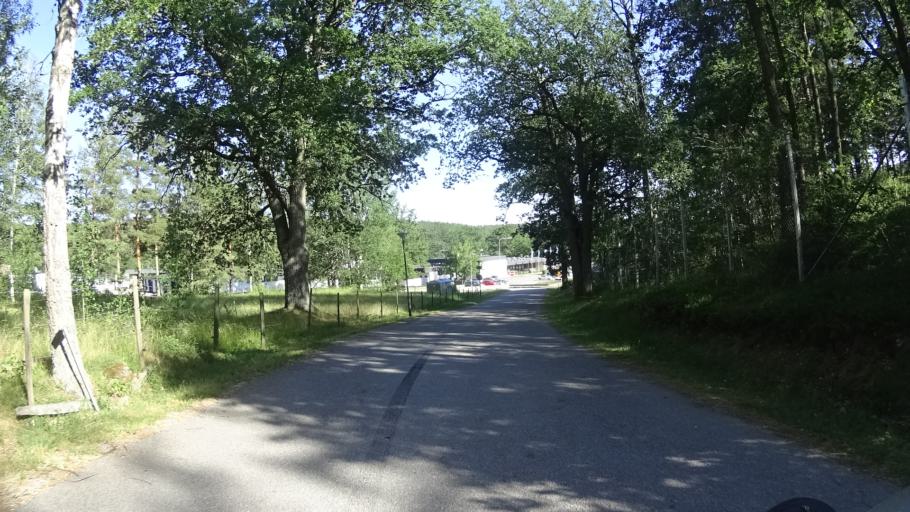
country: SE
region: Kalmar
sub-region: Vasterviks Kommun
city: Gamleby
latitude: 57.9085
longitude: 16.4100
